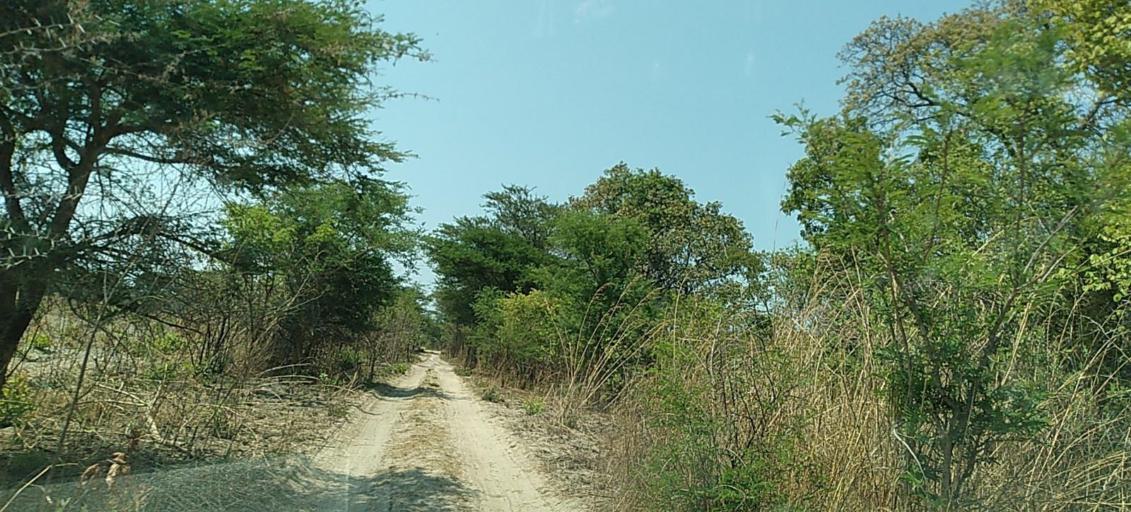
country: ZM
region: Copperbelt
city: Mpongwe
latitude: -13.8358
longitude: 28.0595
